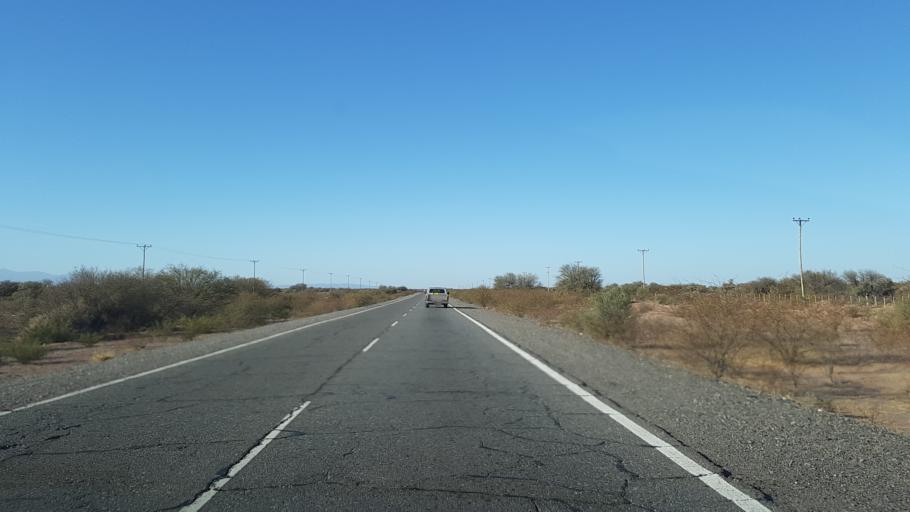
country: AR
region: San Juan
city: Caucete
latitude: -31.6029
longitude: -67.7057
